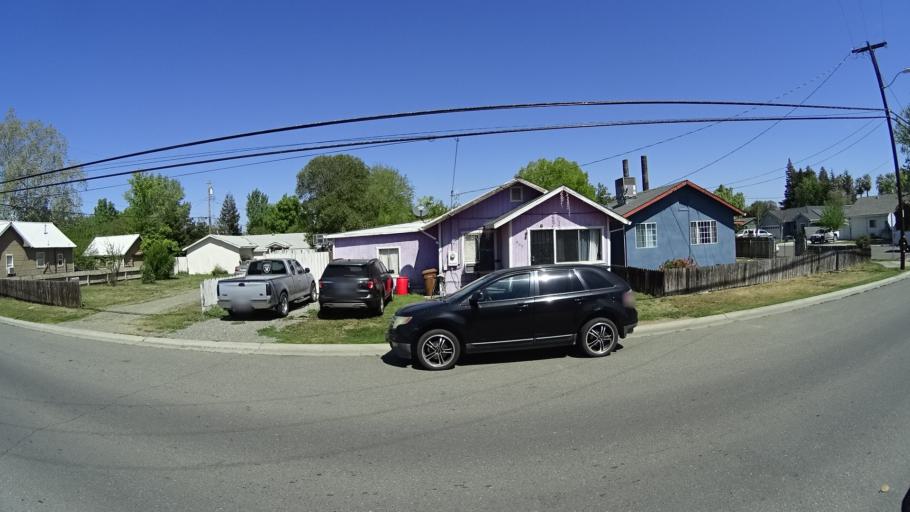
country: US
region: California
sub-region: Glenn County
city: Willows
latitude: 39.5205
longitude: -122.2050
